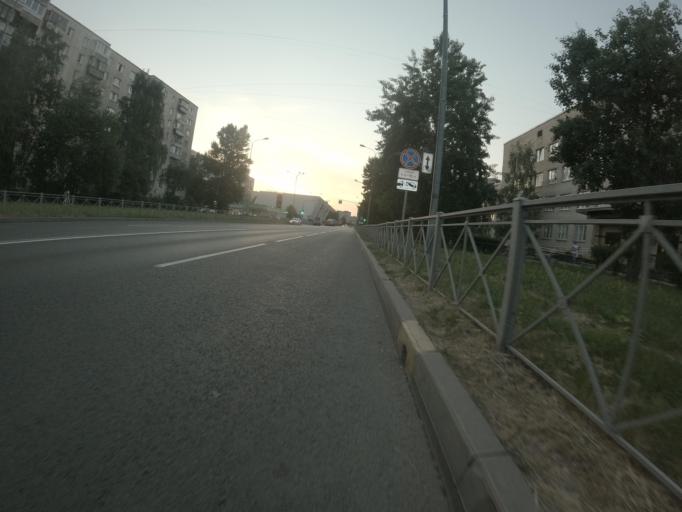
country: RU
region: St.-Petersburg
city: Krasnogvargeisky
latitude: 59.9112
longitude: 30.4618
